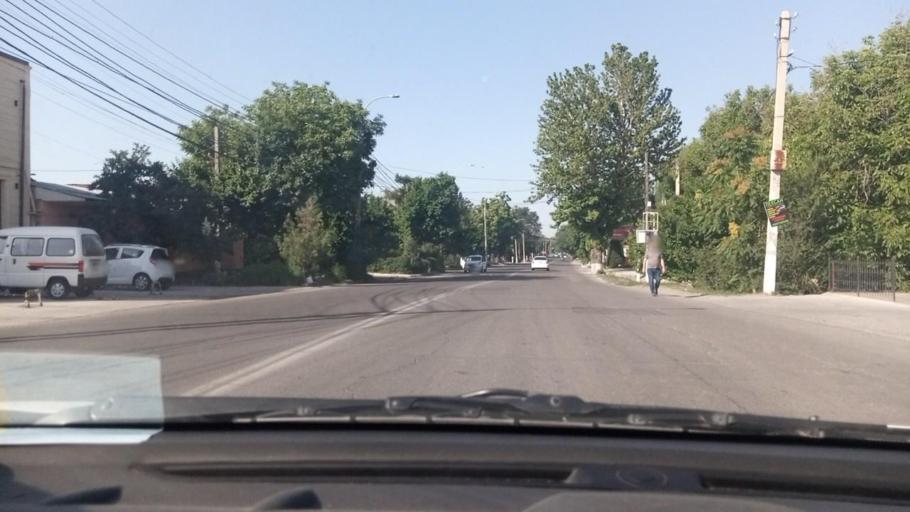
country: UZ
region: Toshkent
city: Salor
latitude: 41.3235
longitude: 69.3470
